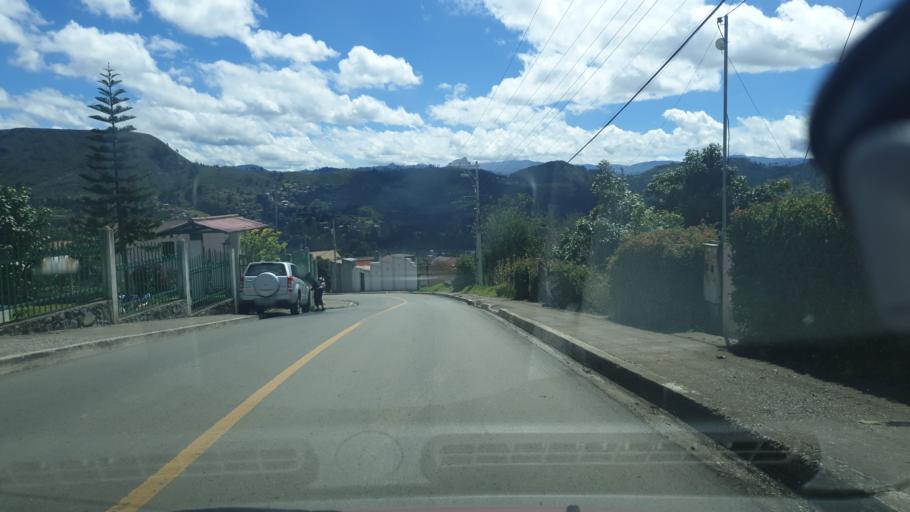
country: EC
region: Azuay
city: Llacao
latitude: -2.8610
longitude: -78.9075
